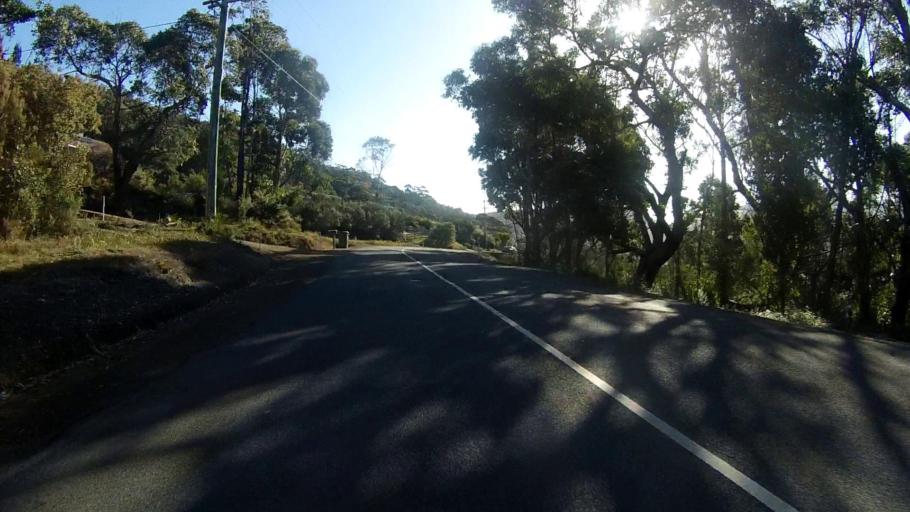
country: AU
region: Tasmania
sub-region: Clarence
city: Sandford
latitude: -43.0287
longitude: 147.9273
